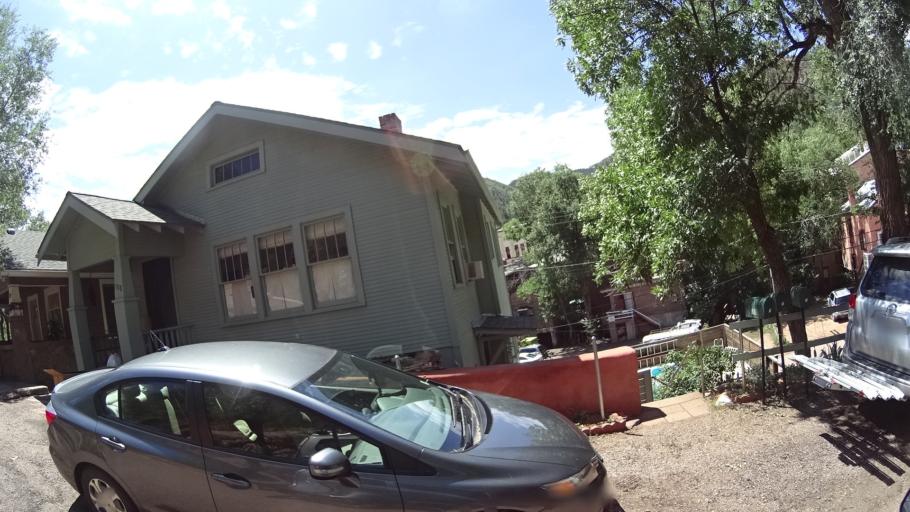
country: US
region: Colorado
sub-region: El Paso County
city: Manitou Springs
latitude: 38.8580
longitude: -104.9154
